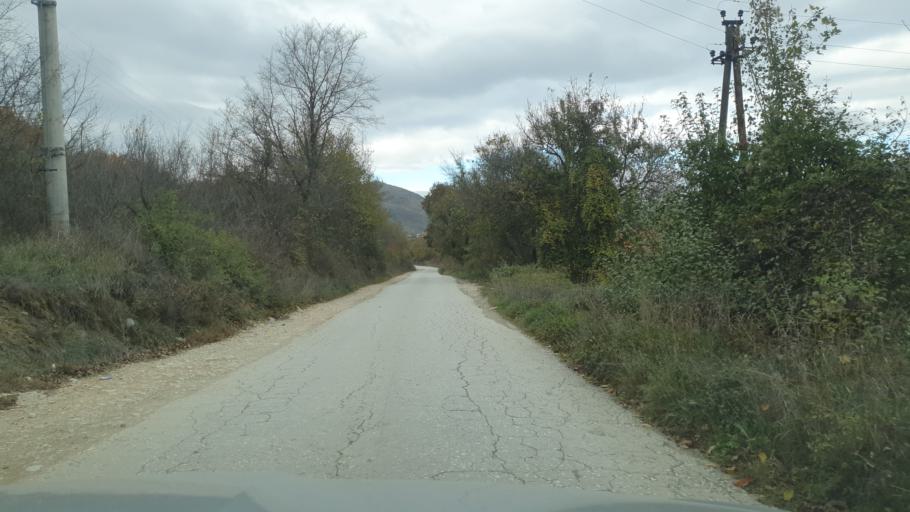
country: MK
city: Kondovo
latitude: 42.0359
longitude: 21.2819
